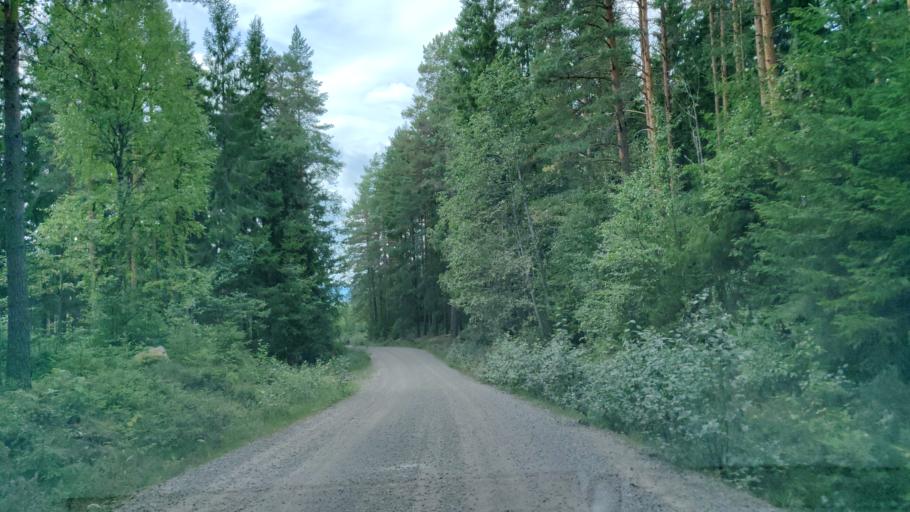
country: SE
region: Vaermland
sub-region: Hagfors Kommun
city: Hagfors
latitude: 60.0057
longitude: 13.7169
